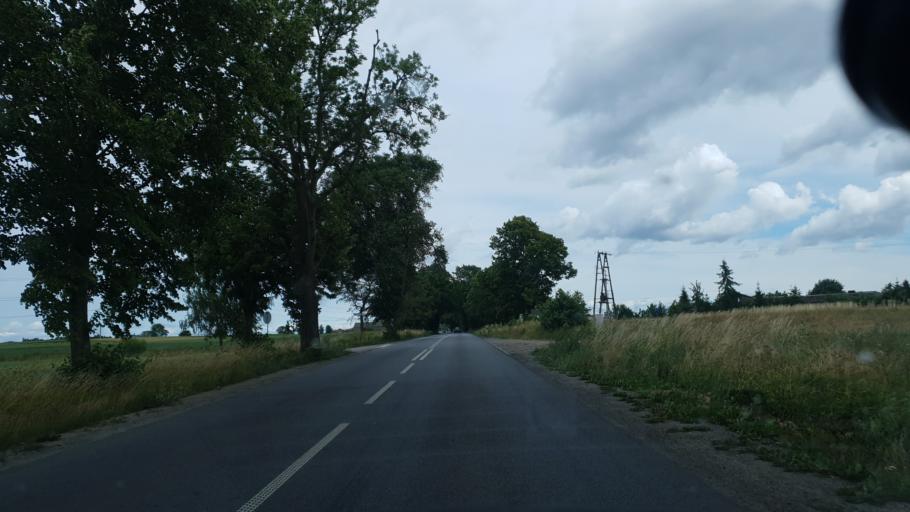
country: PL
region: Pomeranian Voivodeship
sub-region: Powiat kartuski
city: Zukowo
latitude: 54.3823
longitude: 18.3513
